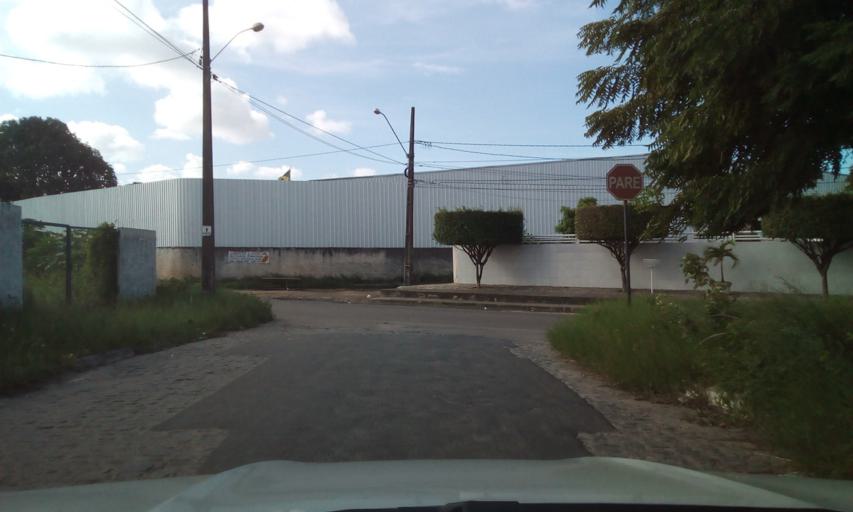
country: BR
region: Paraiba
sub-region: Joao Pessoa
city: Joao Pessoa
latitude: -7.1737
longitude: -34.8664
